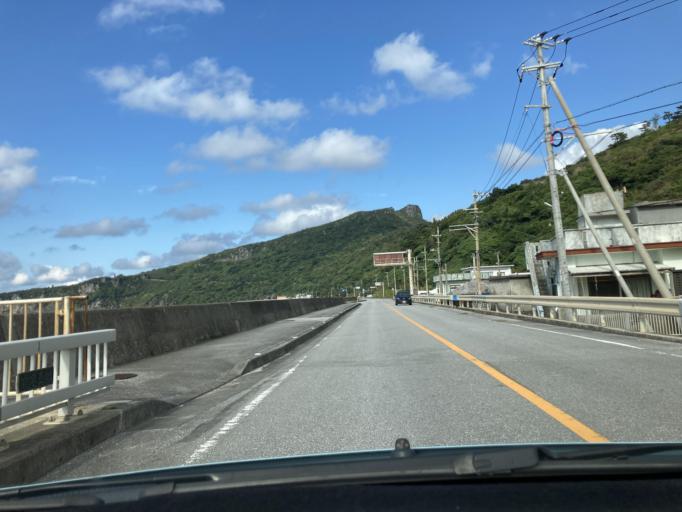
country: JP
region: Okinawa
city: Nago
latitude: 26.8409
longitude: 128.2529
